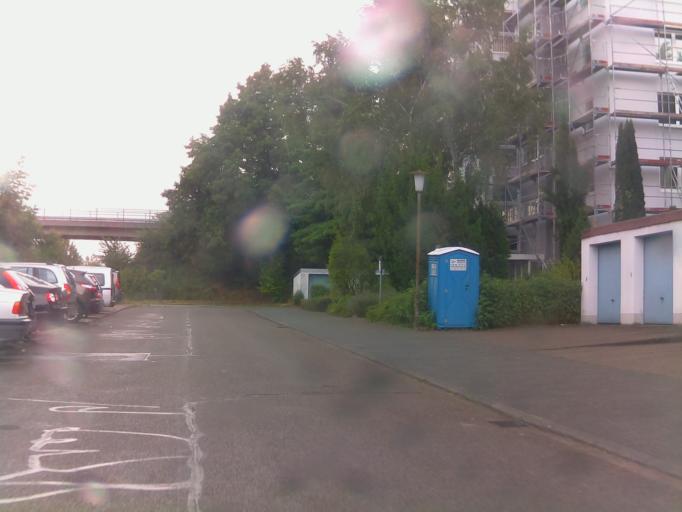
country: DE
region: Hesse
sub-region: Regierungsbezirk Darmstadt
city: Heppenheim an der Bergstrasse
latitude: 49.6346
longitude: 8.6366
